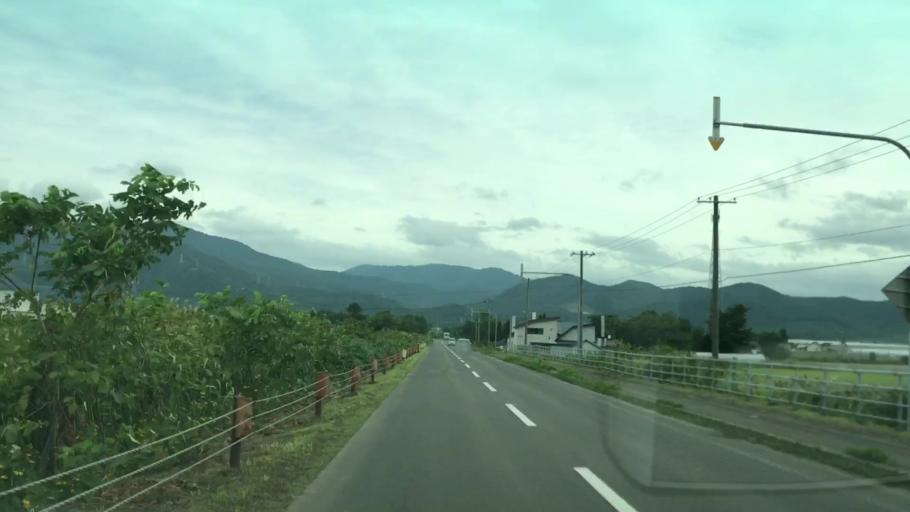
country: JP
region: Hokkaido
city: Iwanai
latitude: 43.0187
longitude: 140.5713
